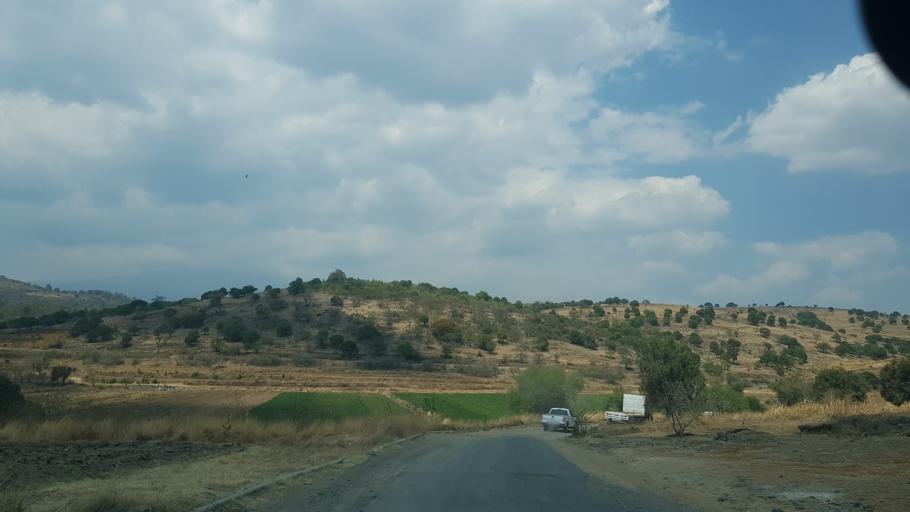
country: MX
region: Puebla
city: San Juan Amecac
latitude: 18.8297
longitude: -98.6221
